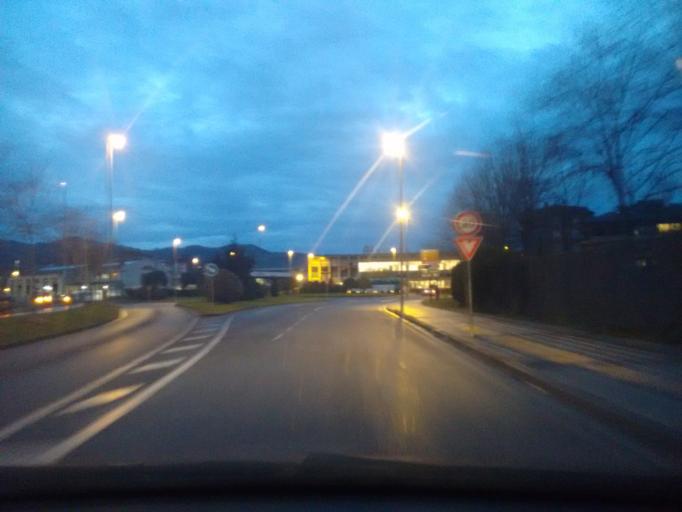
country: ES
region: Basque Country
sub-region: Provincia de Guipuzcoa
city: Zarautz
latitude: 43.2830
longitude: -2.1599
